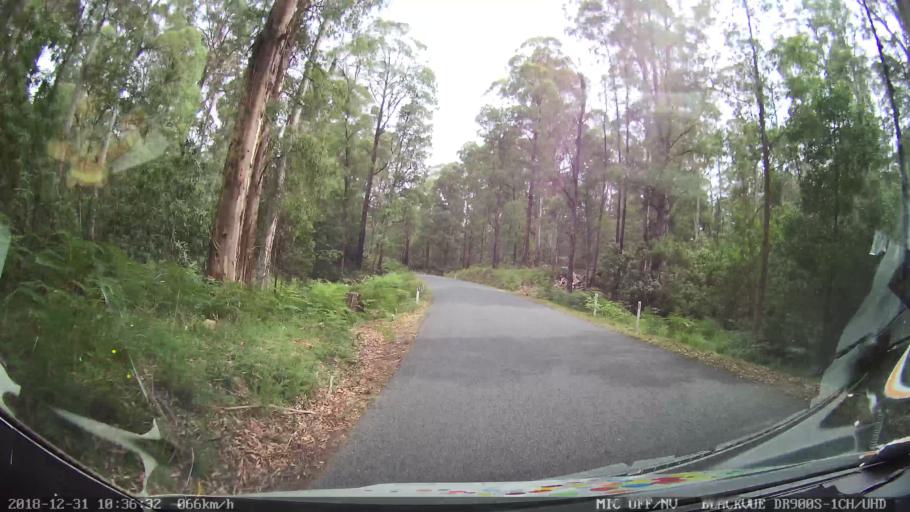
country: AU
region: New South Wales
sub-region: Snowy River
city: Jindabyne
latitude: -36.4253
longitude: 148.1715
